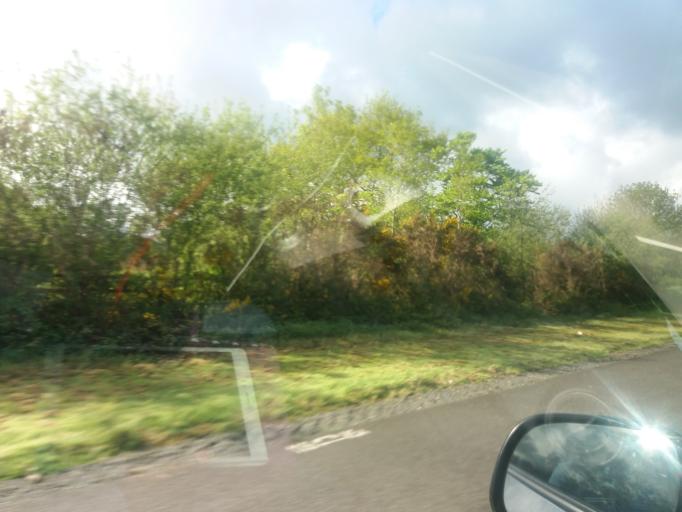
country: IE
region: Leinster
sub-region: Loch Garman
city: Gorey
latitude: 52.6447
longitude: -6.3325
